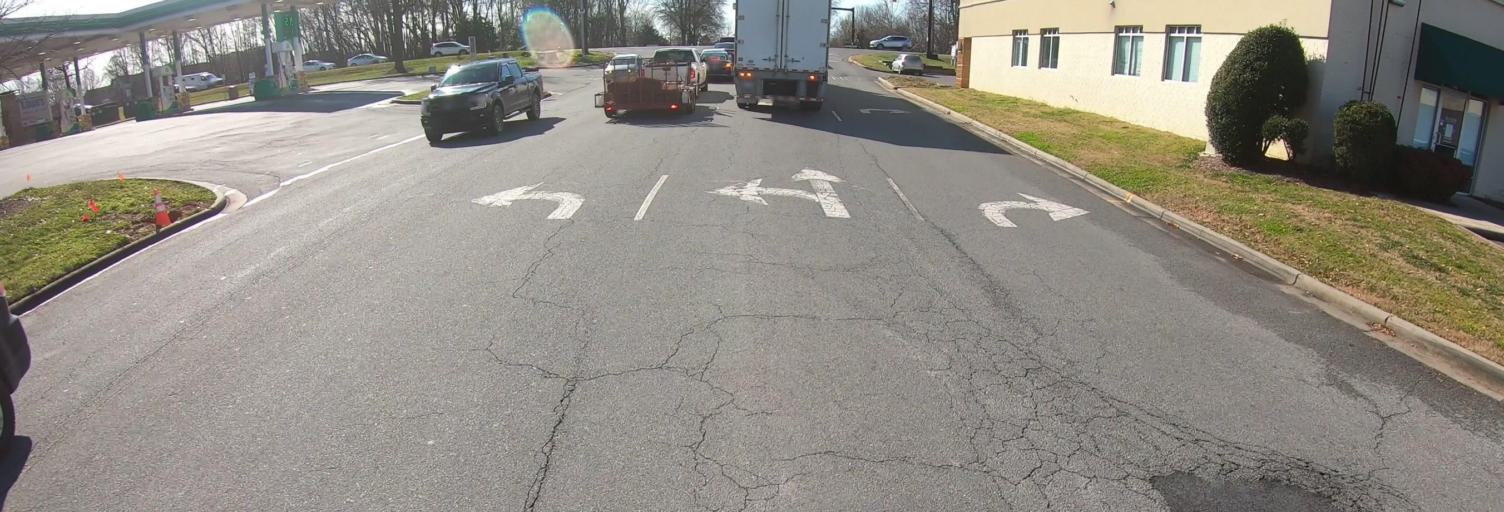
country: US
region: South Carolina
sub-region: York County
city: Fort Mill
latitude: 35.0309
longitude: -80.9666
